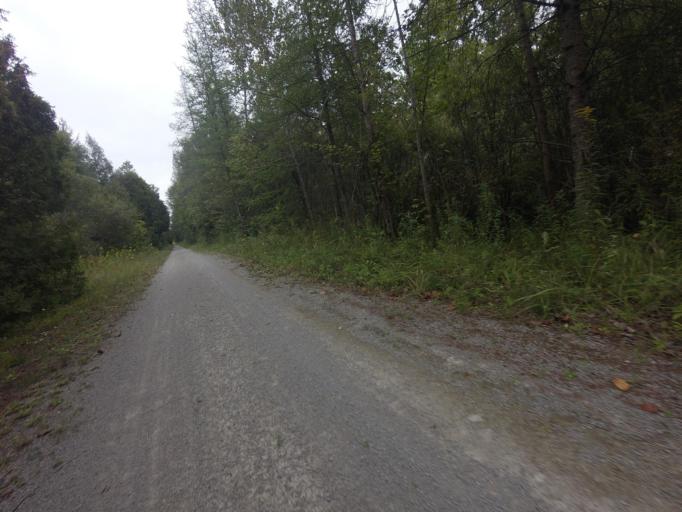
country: CA
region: Ontario
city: Uxbridge
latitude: 44.2938
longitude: -78.9781
